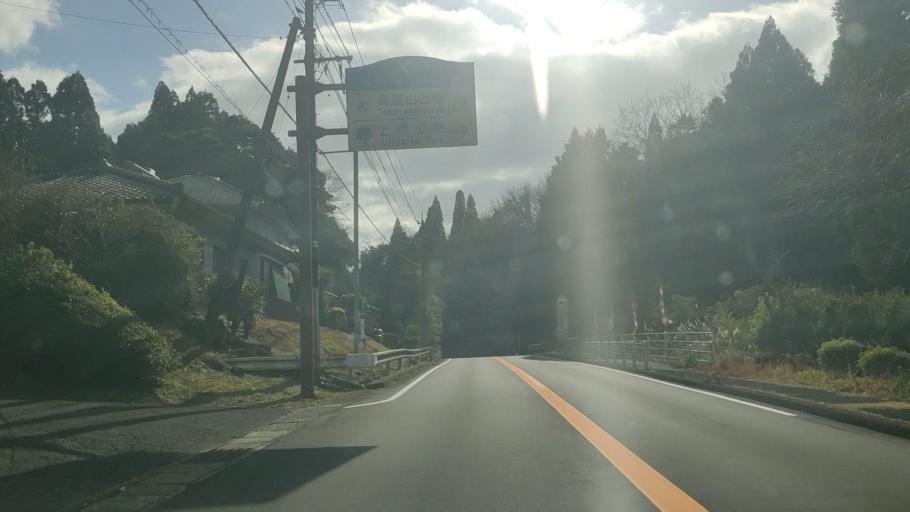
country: JP
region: Kagoshima
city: Kajiki
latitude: 31.8282
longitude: 130.6889
